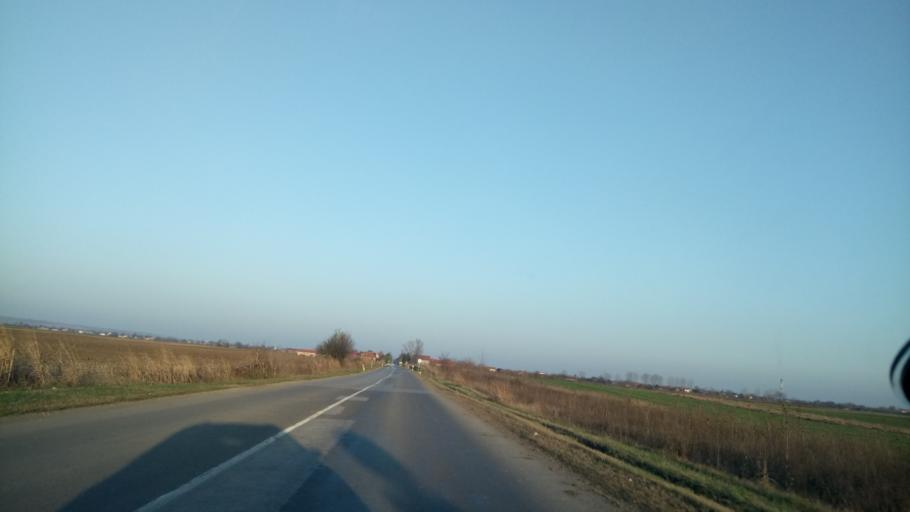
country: RS
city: Novi Karlovci
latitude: 45.0731
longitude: 20.1536
